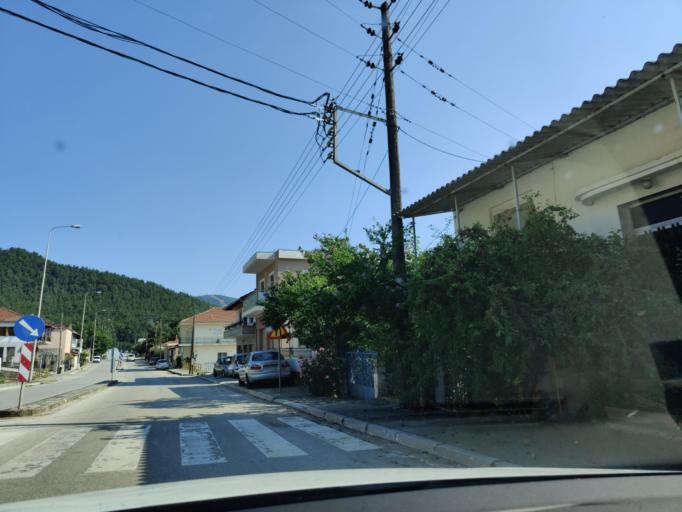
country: GR
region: East Macedonia and Thrace
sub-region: Nomos Kavalas
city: Zygos
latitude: 41.0125
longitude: 24.3816
